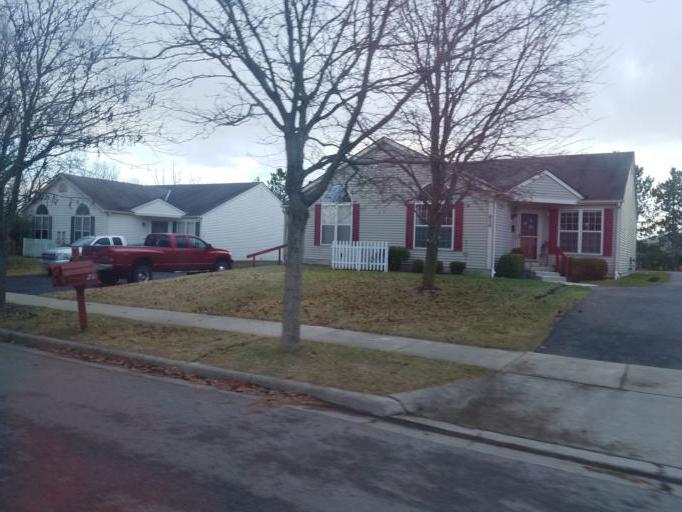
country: US
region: Ohio
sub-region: Delaware County
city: Delaware
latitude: 40.3140
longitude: -83.0974
